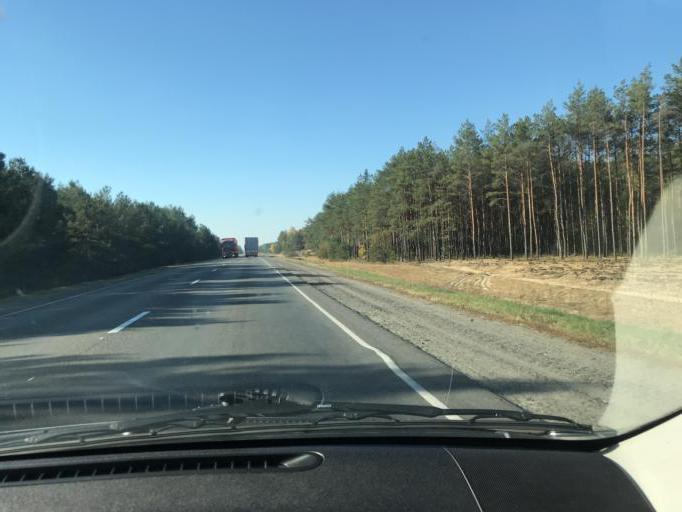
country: BY
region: Brest
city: Davyd-Haradok
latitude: 52.2362
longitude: 27.2343
